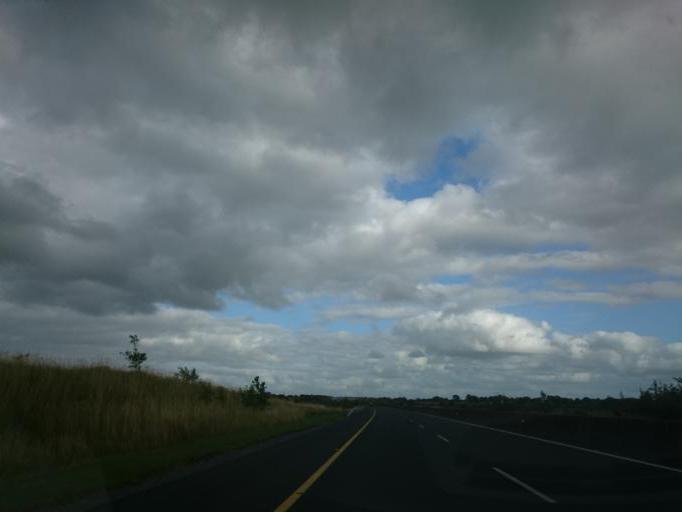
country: IE
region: Connaught
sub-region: County Galway
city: Loughrea
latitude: 53.2676
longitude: -8.6395
